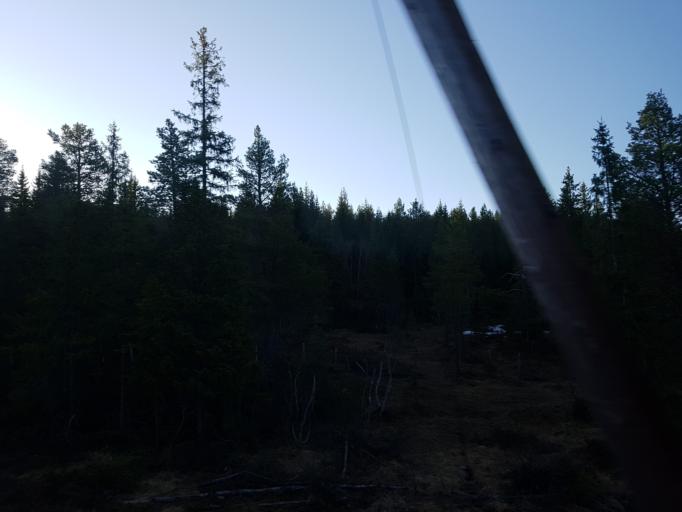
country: NO
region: Sor-Trondelag
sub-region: Rennebu
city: Berkak
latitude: 62.8411
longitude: 10.0216
